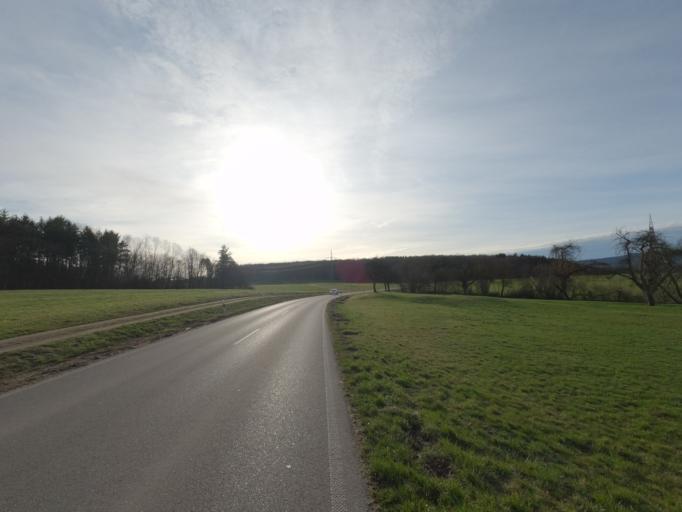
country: DE
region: Baden-Wuerttemberg
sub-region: Regierungsbezirk Stuttgart
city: Hattenhofen
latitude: 48.6778
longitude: 9.5910
